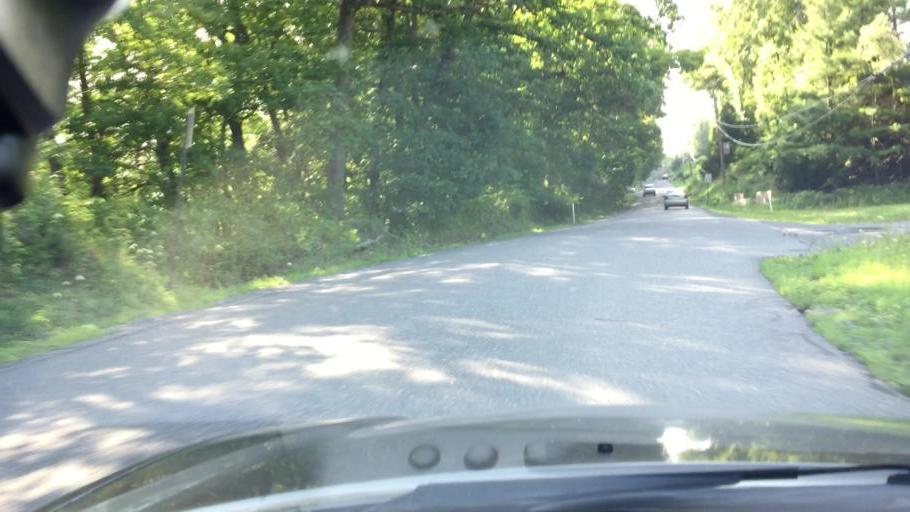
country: US
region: Pennsylvania
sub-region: Carbon County
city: Jim Thorpe
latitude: 40.8732
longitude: -75.7390
